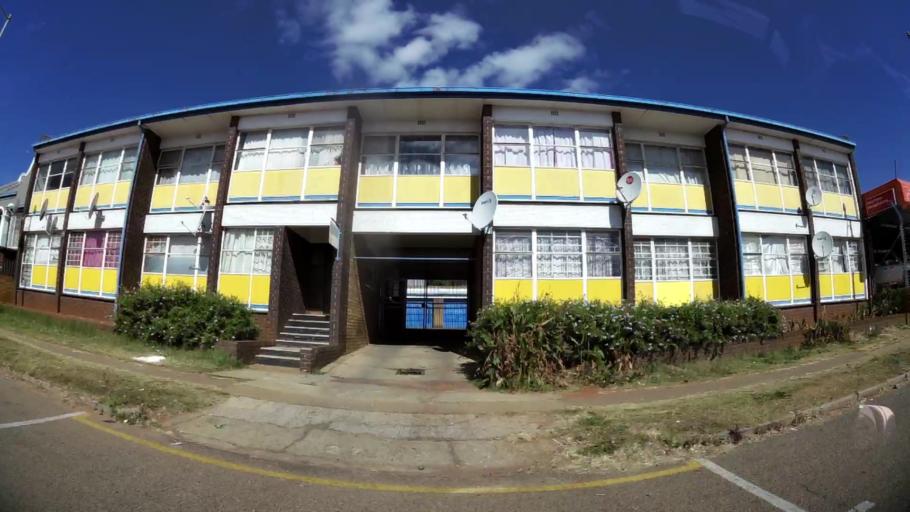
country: ZA
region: Gauteng
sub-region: West Rand District Municipality
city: Krugersdorp
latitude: -26.1078
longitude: 27.7820
